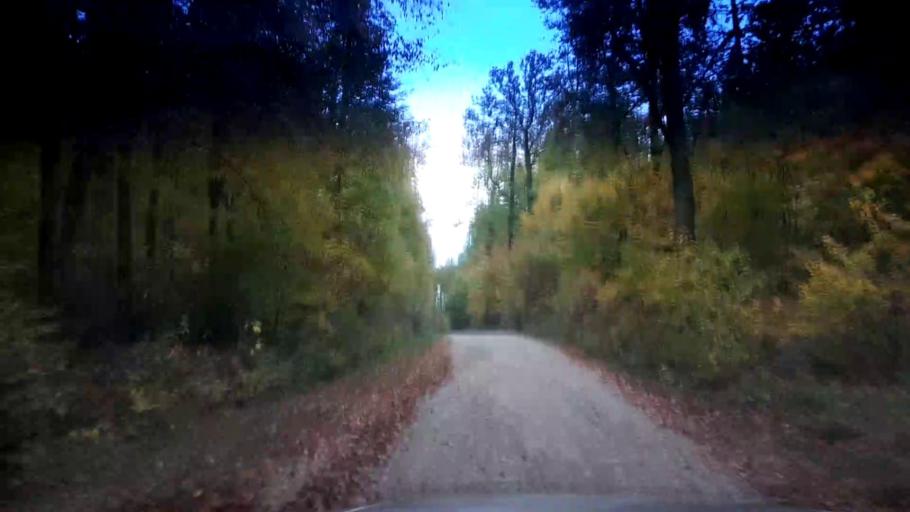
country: DE
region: Bavaria
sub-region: Upper Franconia
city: Schesslitz
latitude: 49.9630
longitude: 11.0313
